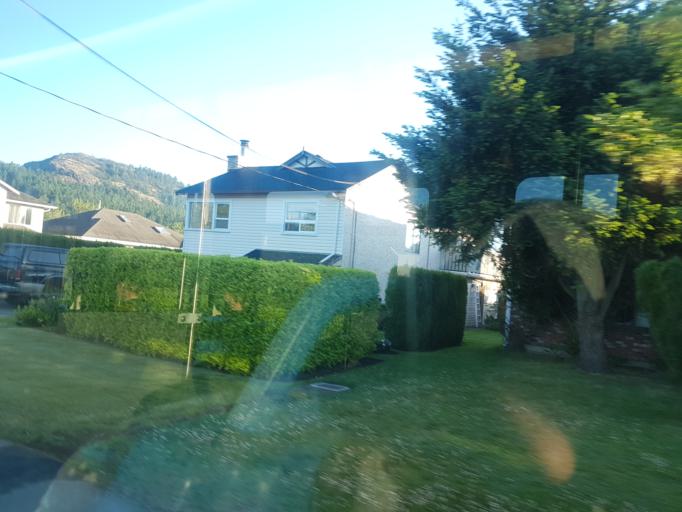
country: CA
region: British Columbia
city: Oak Bay
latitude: 48.4842
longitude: -123.3352
